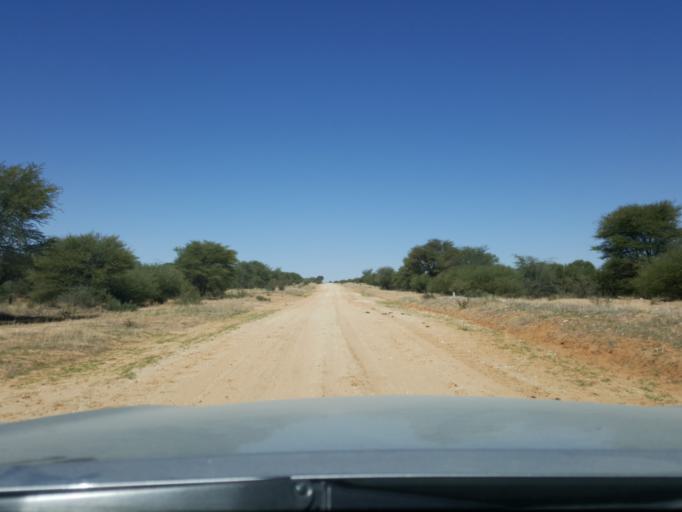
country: BW
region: Kgalagadi
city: Hukuntsi
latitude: -24.0997
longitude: 21.2304
